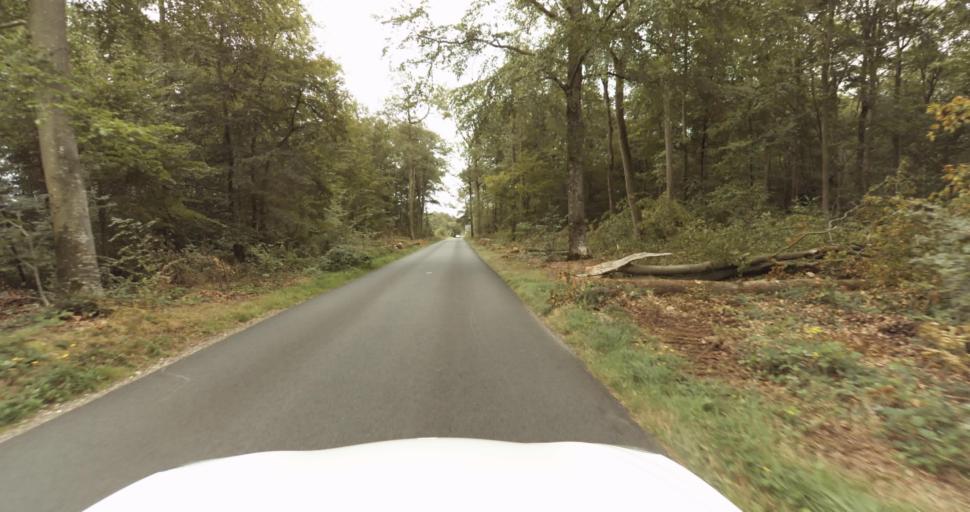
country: FR
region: Haute-Normandie
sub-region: Departement de l'Eure
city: Arnieres-sur-Iton
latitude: 48.9766
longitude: 1.0825
